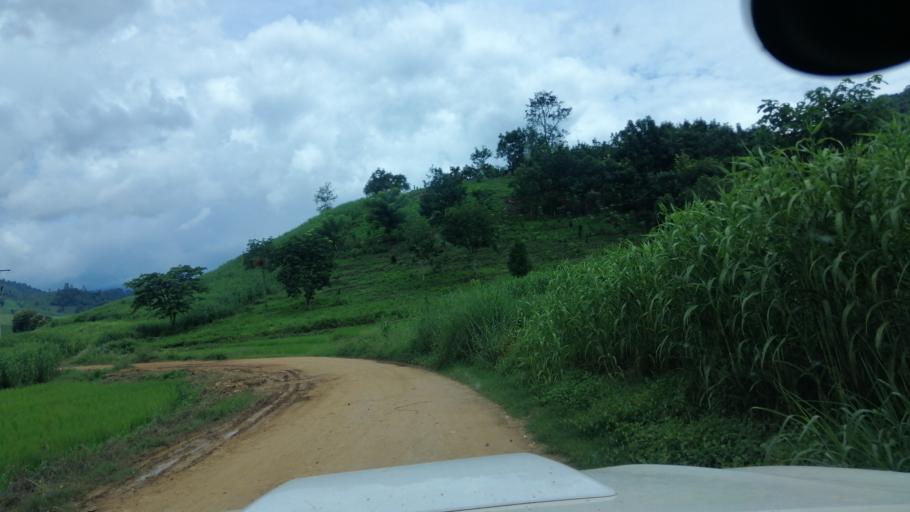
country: TH
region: Phayao
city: Phu Sang
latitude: 19.6966
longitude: 100.4970
